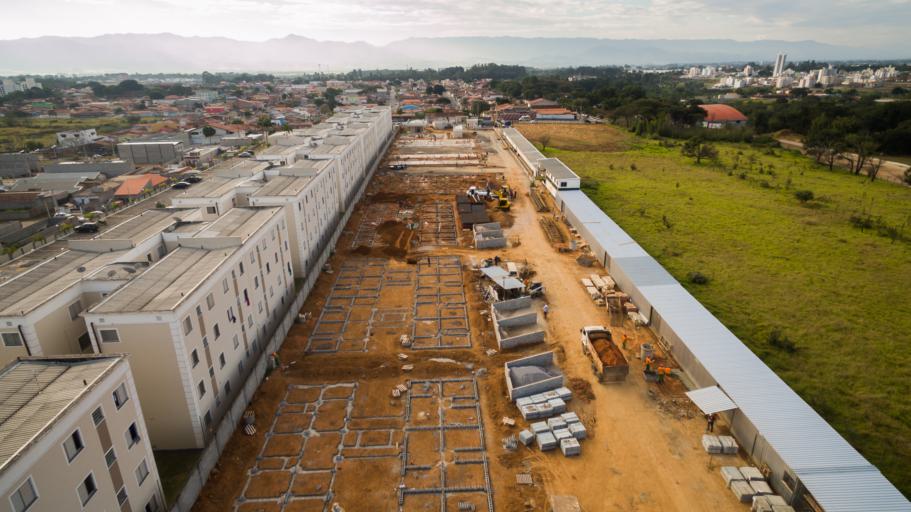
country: BR
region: Sao Paulo
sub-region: Taubate
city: Taubate
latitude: -23.0393
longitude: -45.6008
